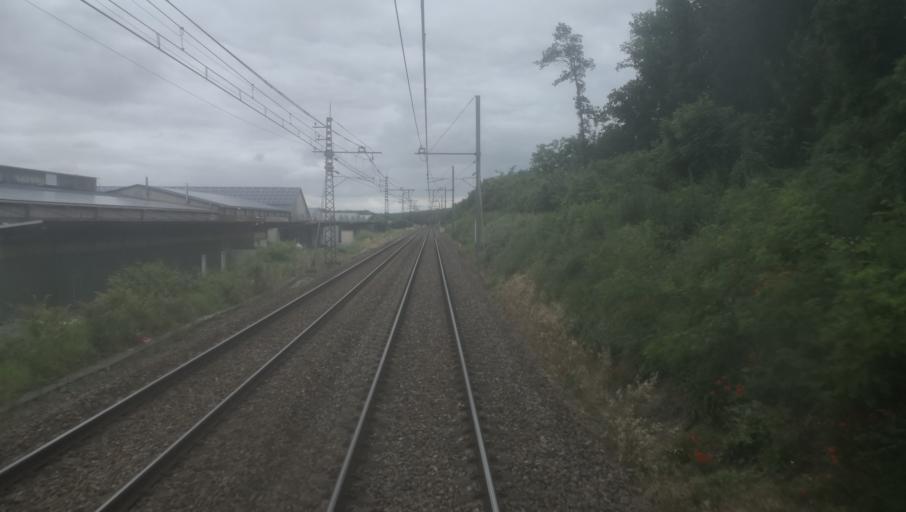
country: FR
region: Midi-Pyrenees
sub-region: Departement du Tarn-et-Garonne
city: Verdun-sur-Garonne
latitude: 43.8849
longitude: 1.2708
